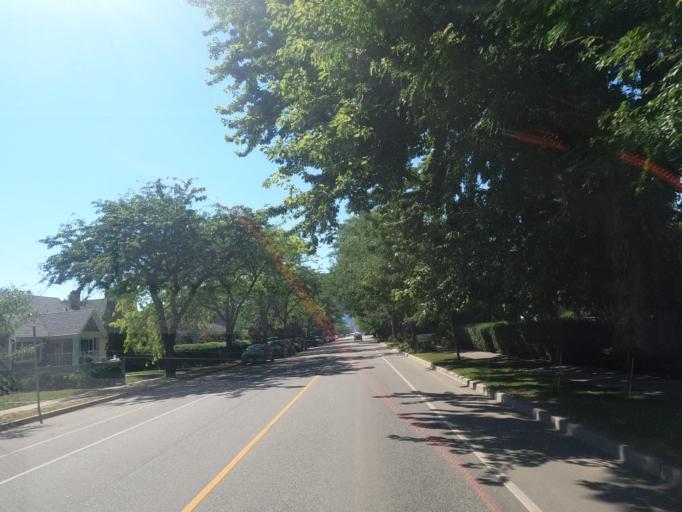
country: CA
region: British Columbia
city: Kelowna
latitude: 49.8864
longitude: -119.4852
